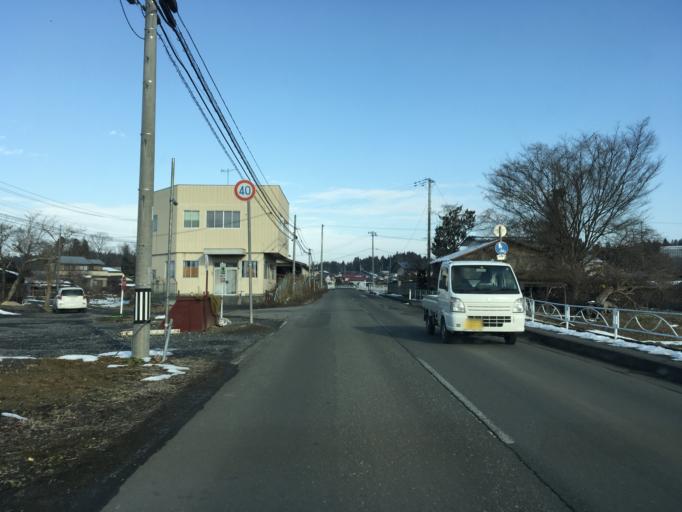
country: JP
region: Iwate
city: Ichinoseki
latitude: 38.8494
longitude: 141.1720
